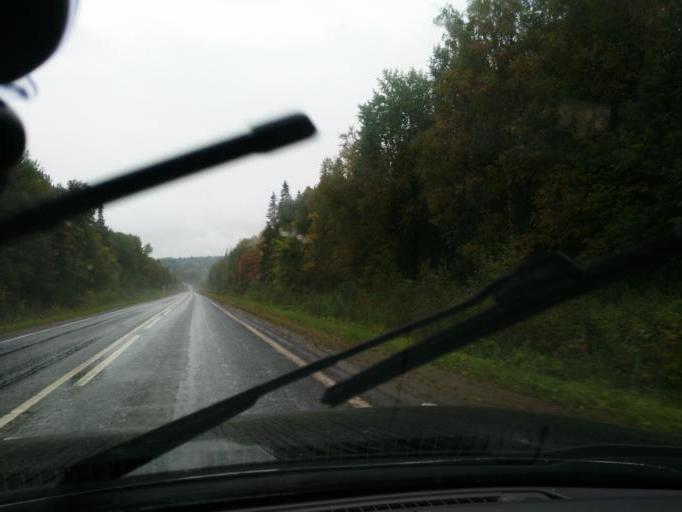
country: RU
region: Perm
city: Yugo-Kamskiy
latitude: 57.5850
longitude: 55.6743
